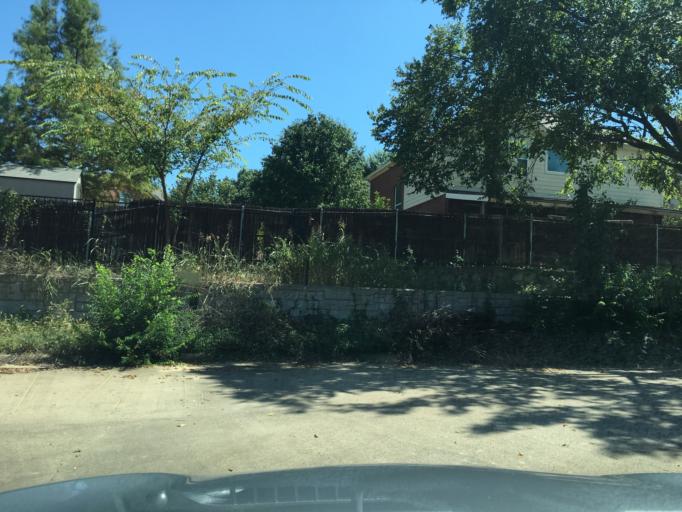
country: US
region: Texas
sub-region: Dallas County
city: Garland
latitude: 32.9527
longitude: -96.6445
